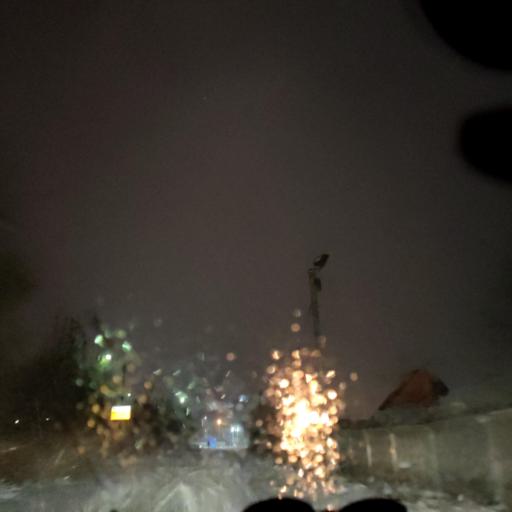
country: RU
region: Voronezj
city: Voronezh
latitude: 51.6692
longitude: 39.1279
